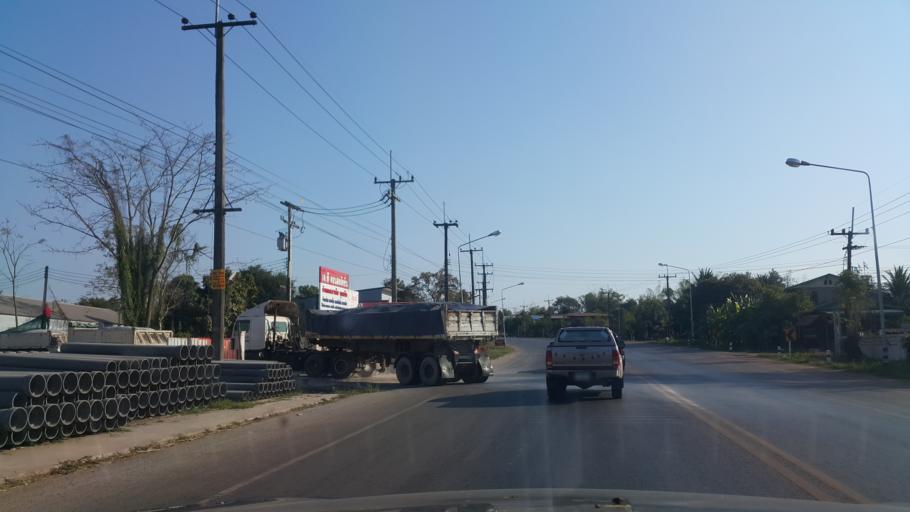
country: TH
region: Changwat Udon Thani
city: Nong Han
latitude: 17.3314
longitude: 103.1092
